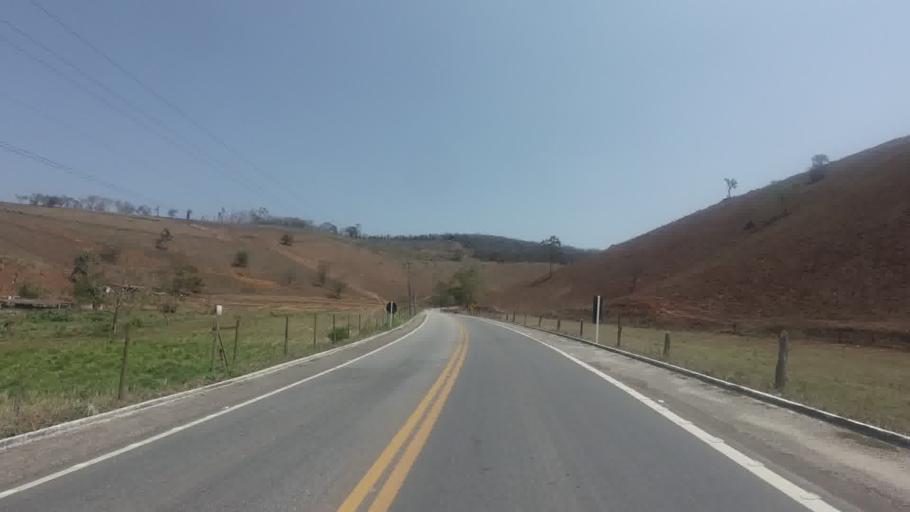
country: BR
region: Espirito Santo
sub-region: Cachoeiro De Itapemirim
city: Cachoeiro de Itapemirim
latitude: -20.8261
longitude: -41.1877
